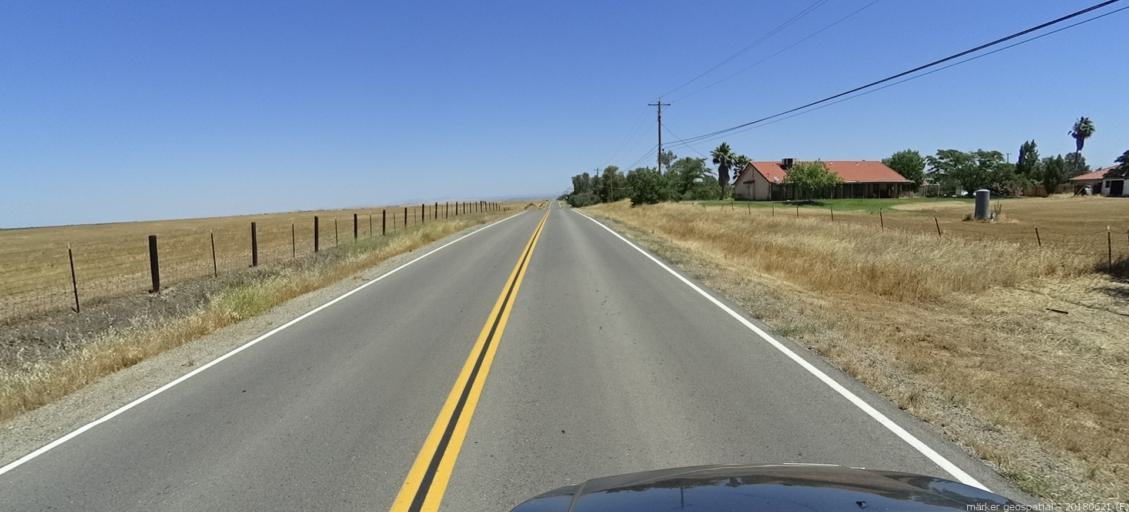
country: US
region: California
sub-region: Madera County
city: Bonadelle Ranchos-Madera Ranchos
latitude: 36.9795
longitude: -119.8938
